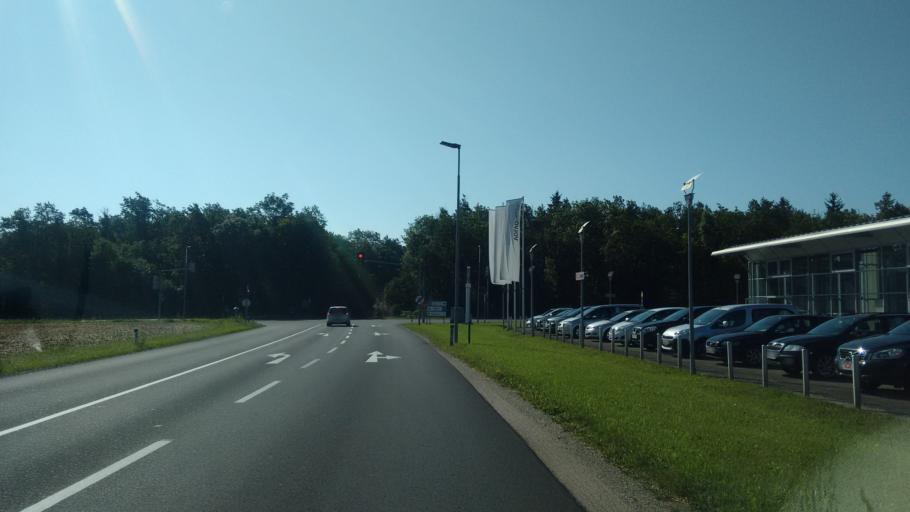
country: AT
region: Upper Austria
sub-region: Wels-Land
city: Gunskirchen
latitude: 48.1320
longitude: 13.9577
